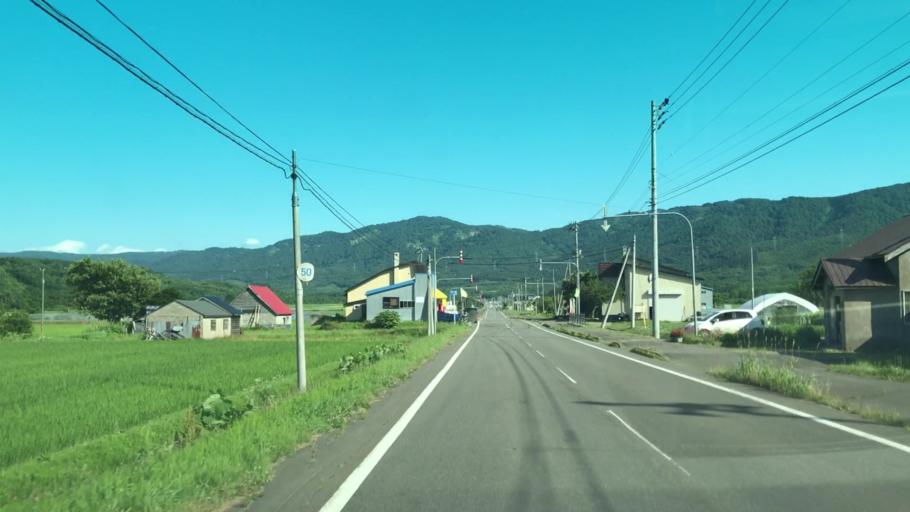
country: JP
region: Hokkaido
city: Yoichi
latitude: 43.0543
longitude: 140.7188
